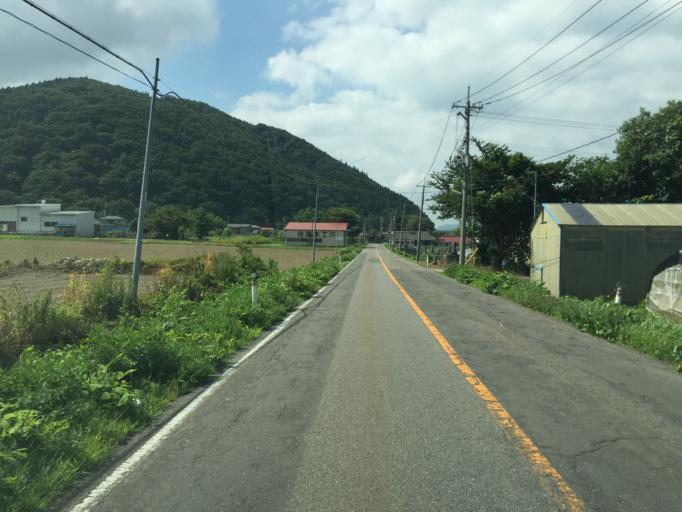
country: JP
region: Fukushima
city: Inawashiro
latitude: 37.4417
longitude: 140.1515
